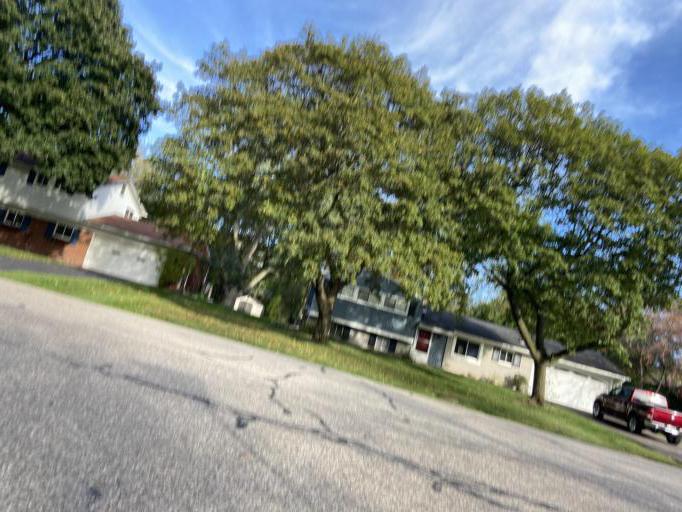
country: US
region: Michigan
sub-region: Oakland County
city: Farmington Hills
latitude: 42.5125
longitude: -83.3685
